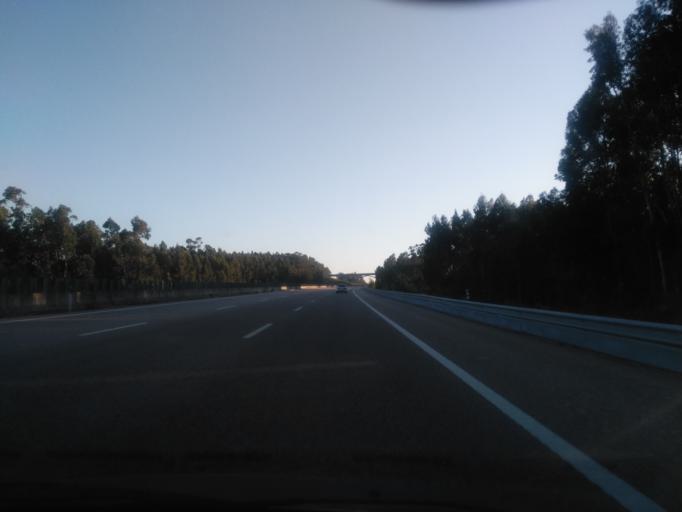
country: PT
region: Coimbra
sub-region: Figueira da Foz
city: Lavos
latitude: 40.0852
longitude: -8.7668
